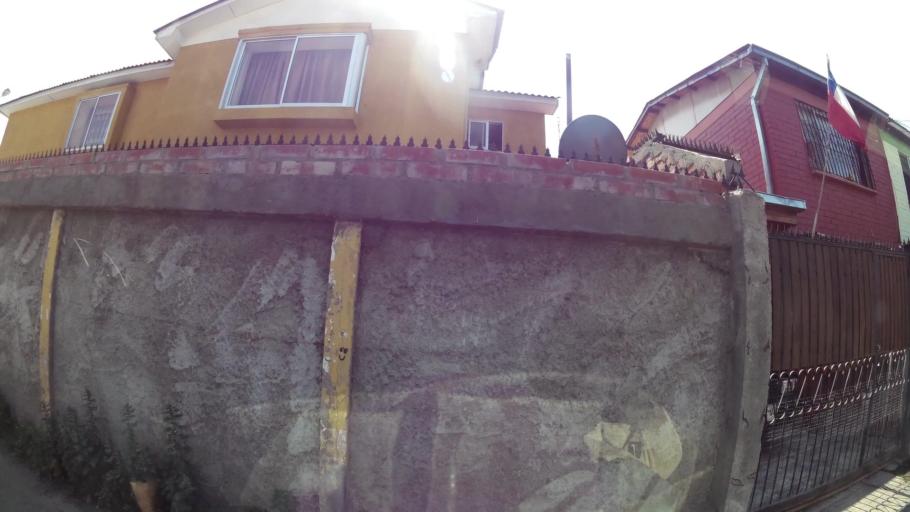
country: CL
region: Santiago Metropolitan
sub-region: Provincia de Santiago
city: La Pintana
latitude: -33.5476
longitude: -70.6174
